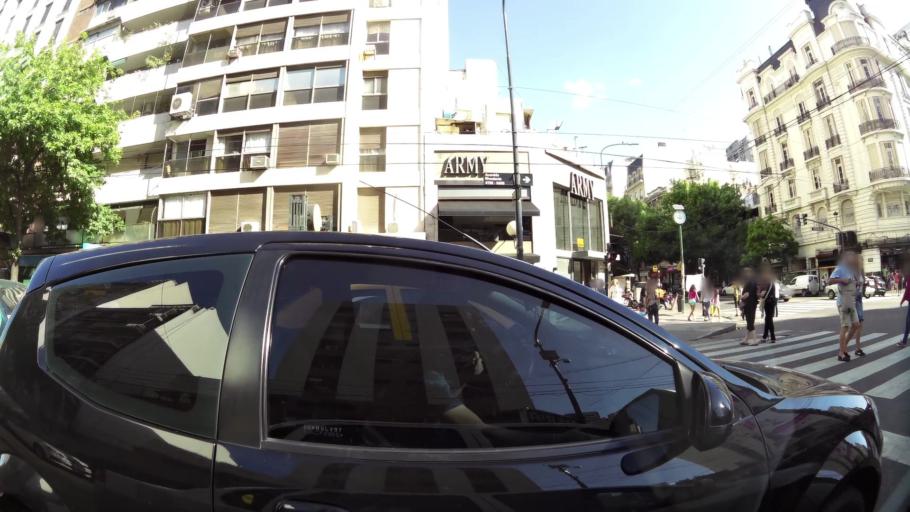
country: AR
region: Buenos Aires F.D.
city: Villa Santa Rita
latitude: -34.6183
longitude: -58.4363
